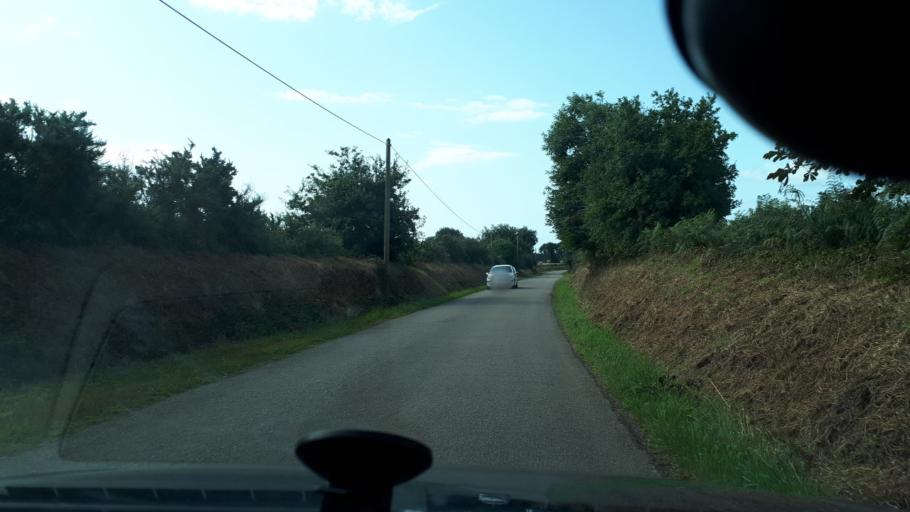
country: FR
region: Brittany
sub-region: Departement du Finistere
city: Landudec
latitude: 47.9964
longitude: -4.3644
